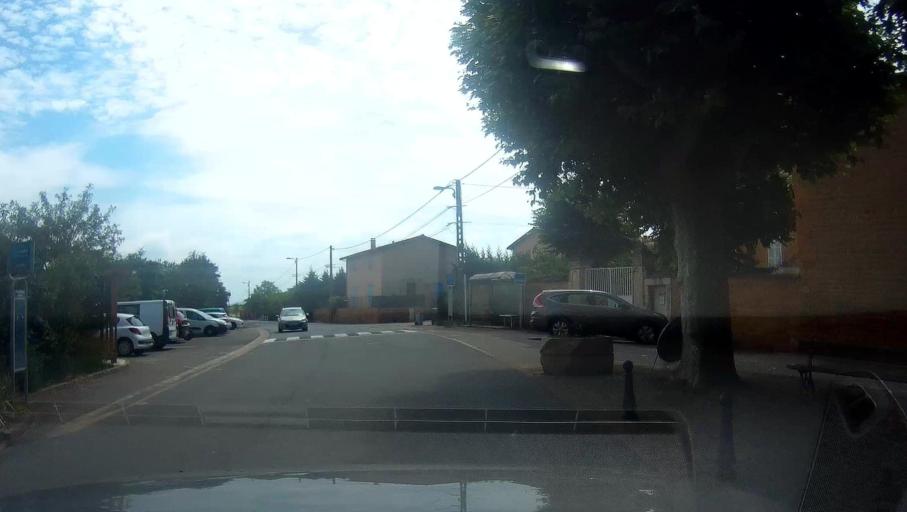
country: FR
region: Rhone-Alpes
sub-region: Departement du Rhone
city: Theize
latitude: 45.9245
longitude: 4.6184
